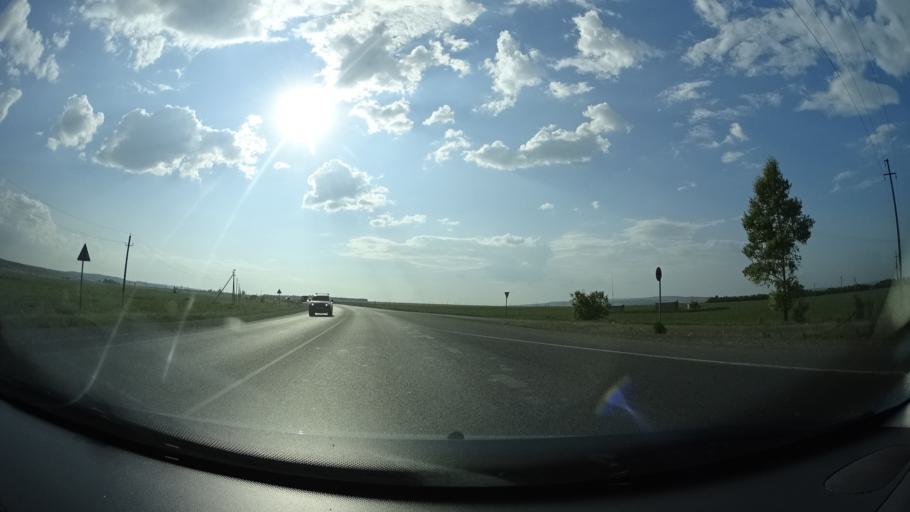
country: RU
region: Bashkortostan
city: Oktyabr'skiy
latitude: 54.4821
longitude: 53.3851
